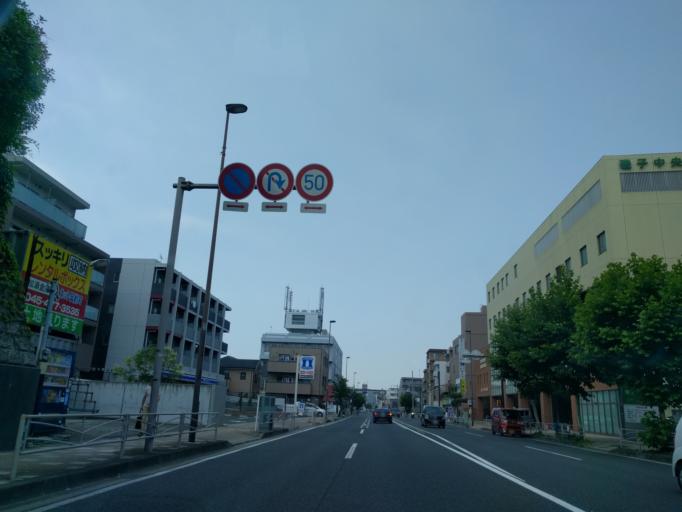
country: JP
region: Kanagawa
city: Yokohama
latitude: 35.4068
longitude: 139.6208
